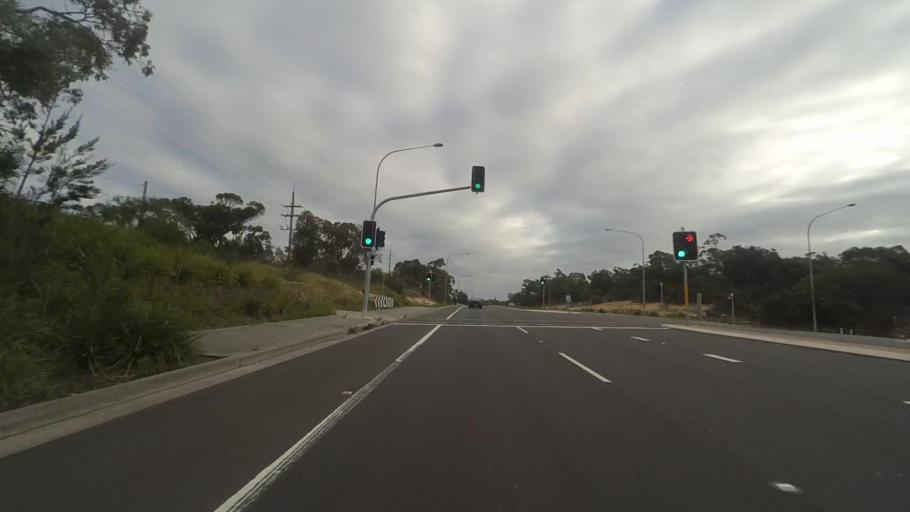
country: AU
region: New South Wales
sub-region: Sutherland Shire
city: Menai
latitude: -34.0282
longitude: 151.0066
